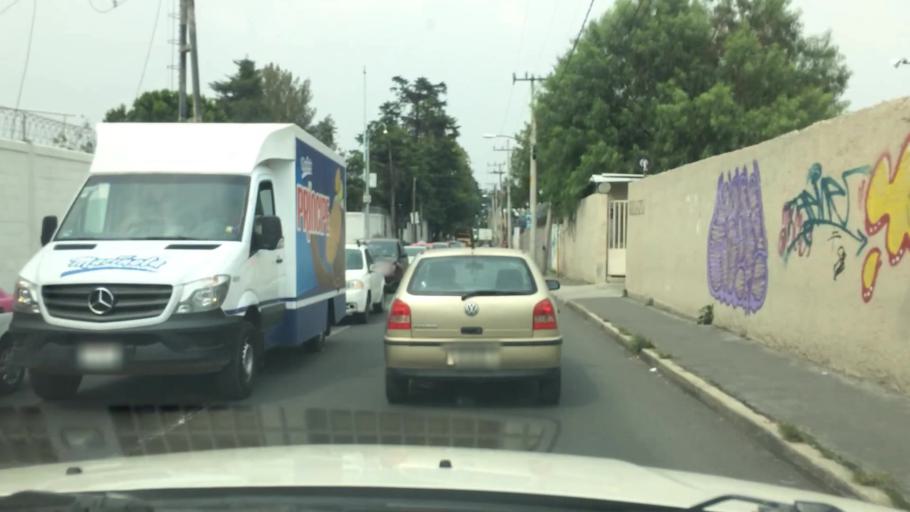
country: MX
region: Mexico City
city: Xochimilco
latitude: 19.2694
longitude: -99.1271
